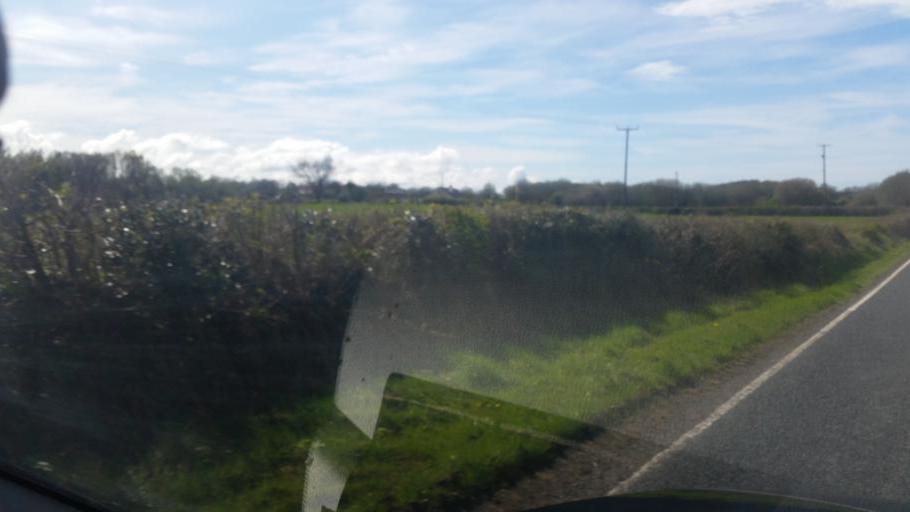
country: IE
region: Ulster
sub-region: County Donegal
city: Ballyshannon
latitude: 54.4690
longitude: -8.0525
